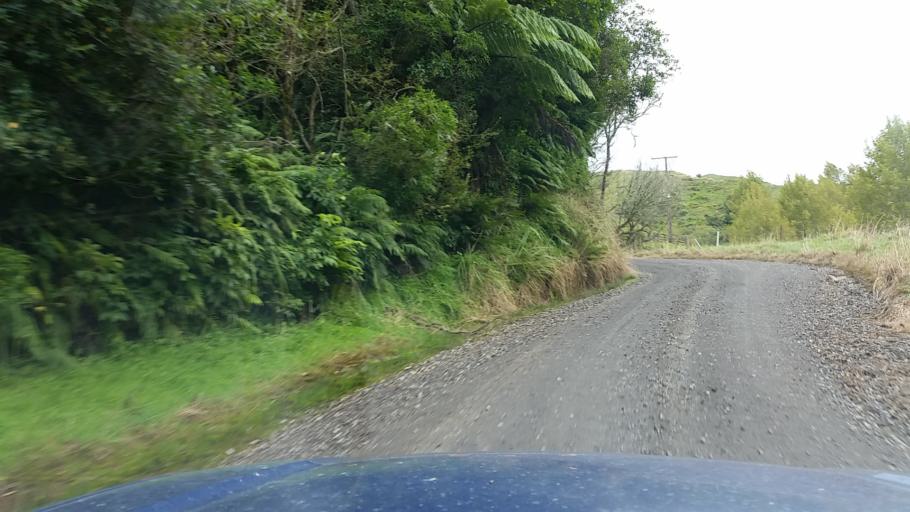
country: NZ
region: Taranaki
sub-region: South Taranaki District
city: Eltham
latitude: -39.2634
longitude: 174.4136
